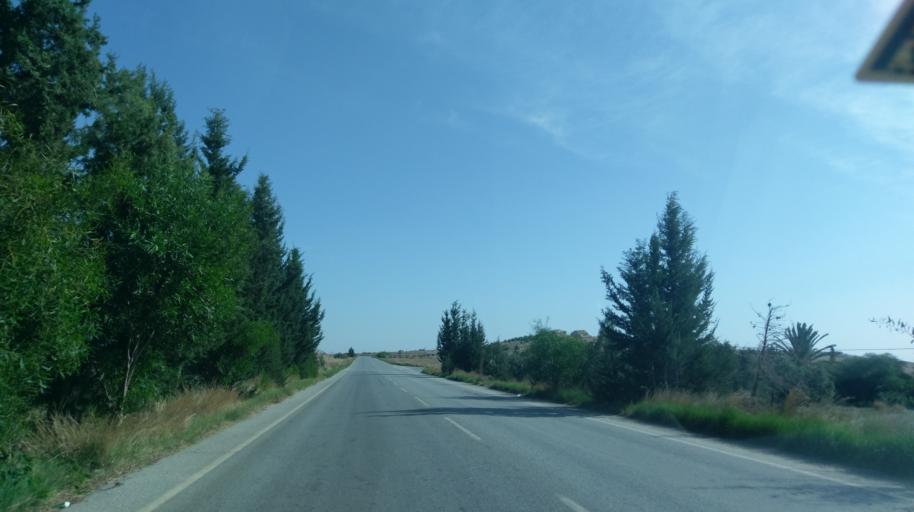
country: CY
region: Ammochostos
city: Lefkonoiko
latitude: 35.2508
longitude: 33.6229
